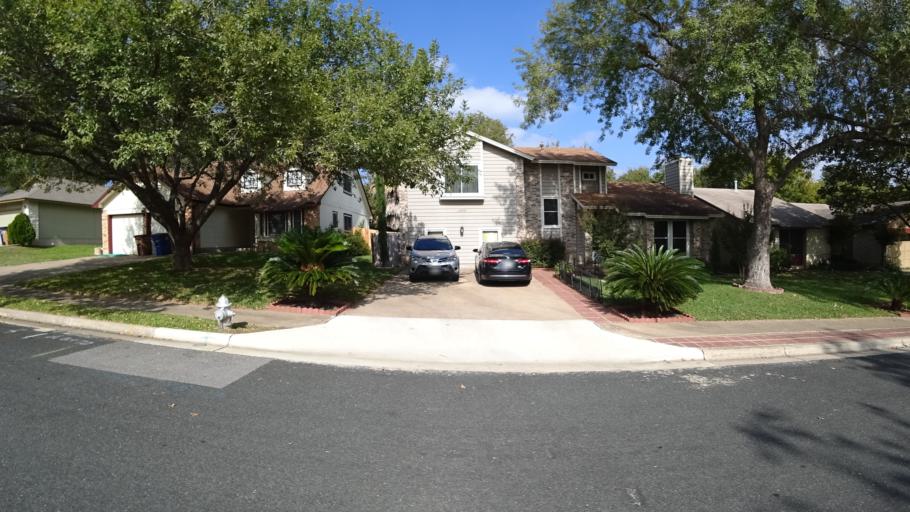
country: US
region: Texas
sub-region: Travis County
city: Shady Hollow
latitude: 30.2003
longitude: -97.8236
